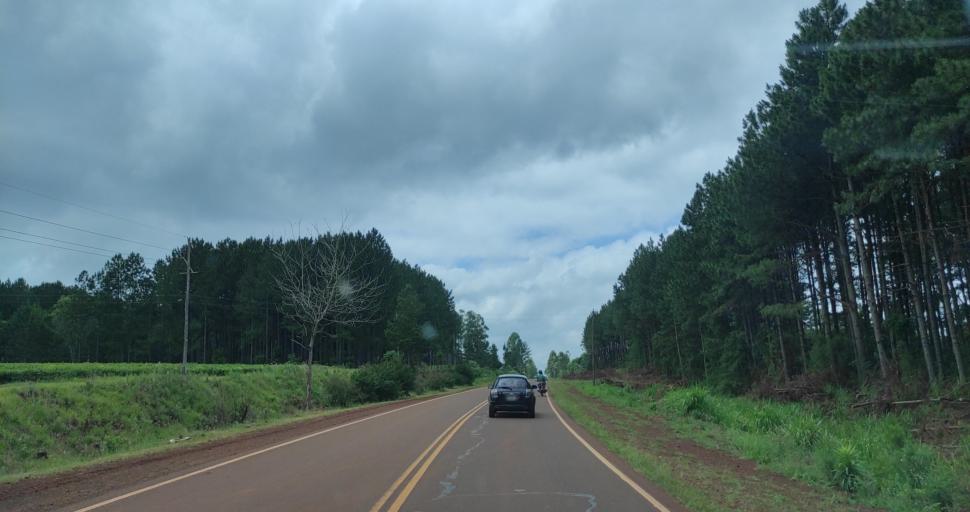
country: AR
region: Misiones
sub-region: Departamento de Veinticinco de Mayo
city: Veinticinco de Mayo
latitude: -27.4124
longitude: -54.7395
